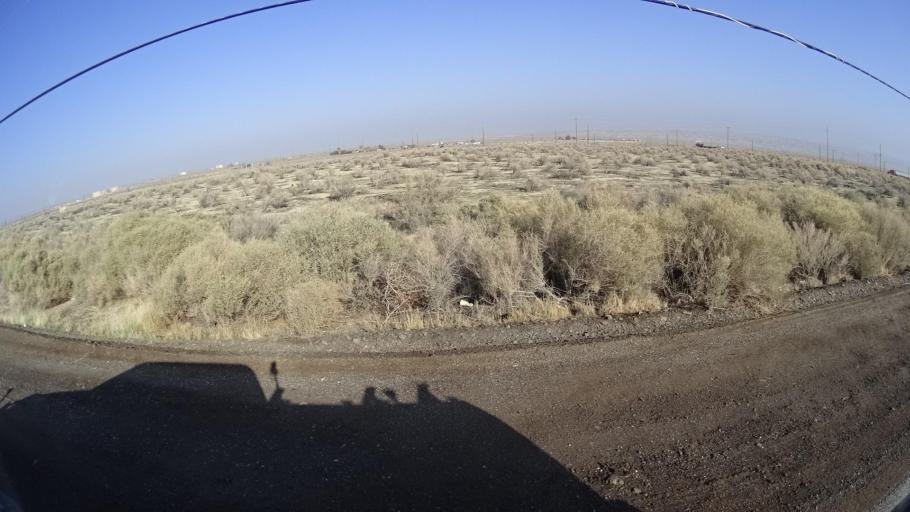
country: US
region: California
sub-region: Kern County
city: Taft Heights
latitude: 35.1801
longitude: -119.5315
